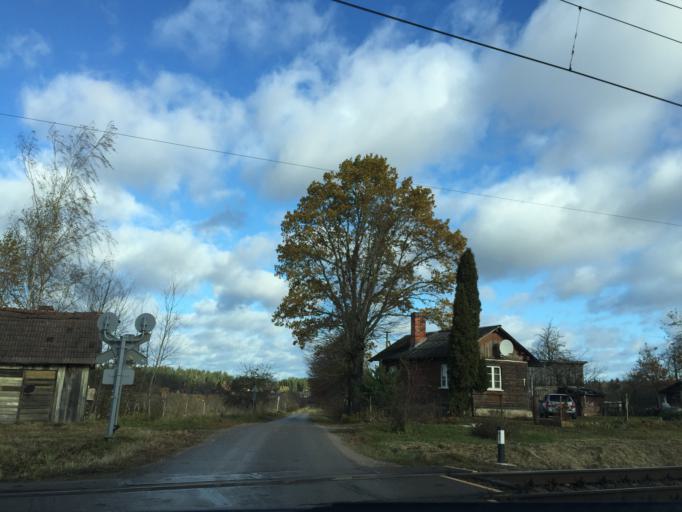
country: LV
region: Tukuma Rajons
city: Tukums
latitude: 56.9700
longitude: 23.2282
